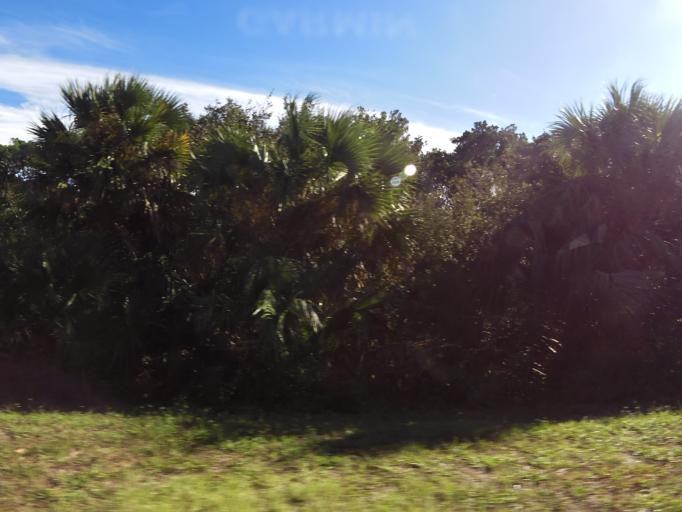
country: US
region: Florida
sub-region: Saint Johns County
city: Saint Augustine Beach
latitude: 29.8620
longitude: -81.2726
